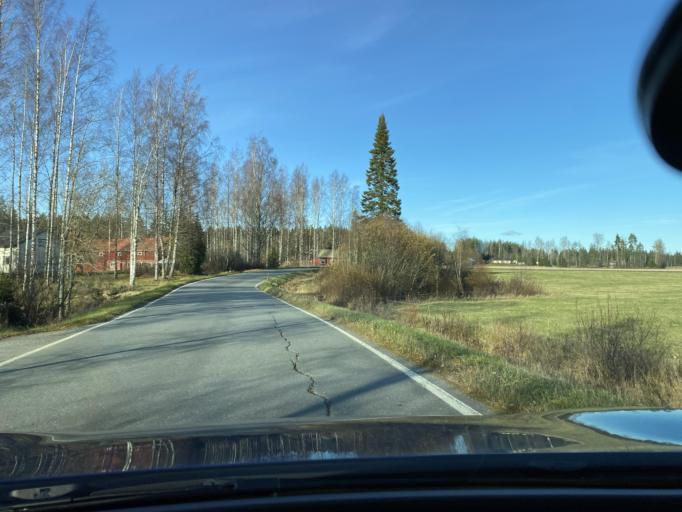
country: FI
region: Haeme
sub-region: Forssa
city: Tammela
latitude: 60.8828
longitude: 23.8451
